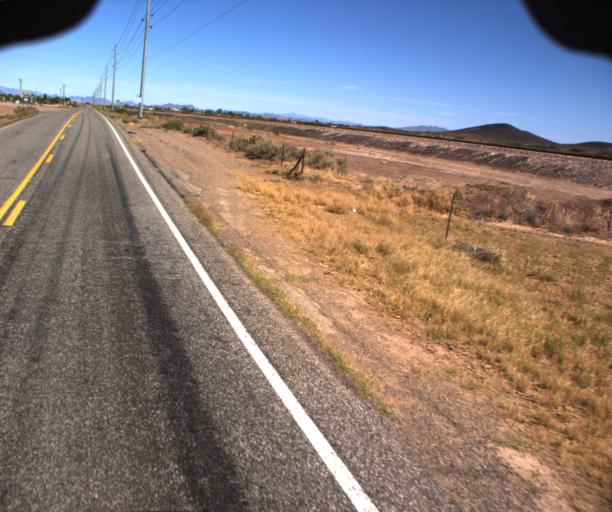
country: US
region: Arizona
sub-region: La Paz County
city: Quartzsite
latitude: 33.9200
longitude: -113.9961
